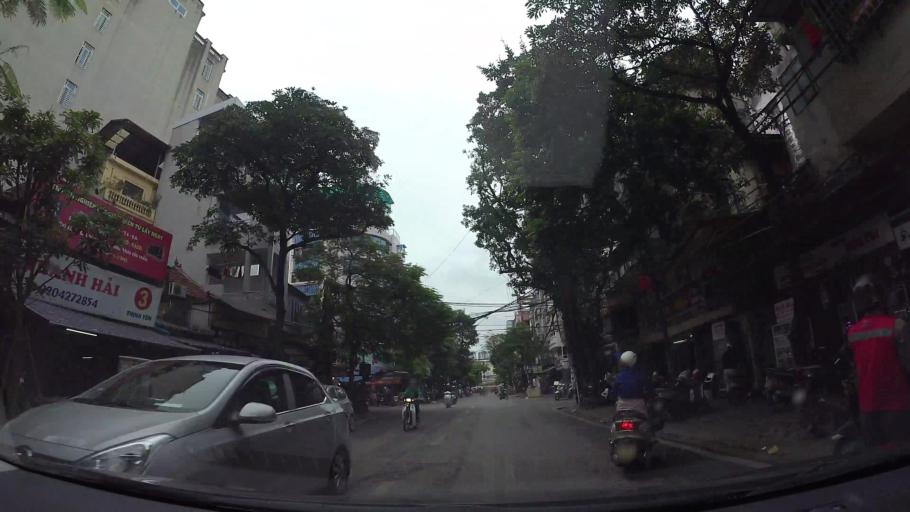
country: VN
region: Ha Noi
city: Hai BaTrung
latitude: 21.0097
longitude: 105.8517
